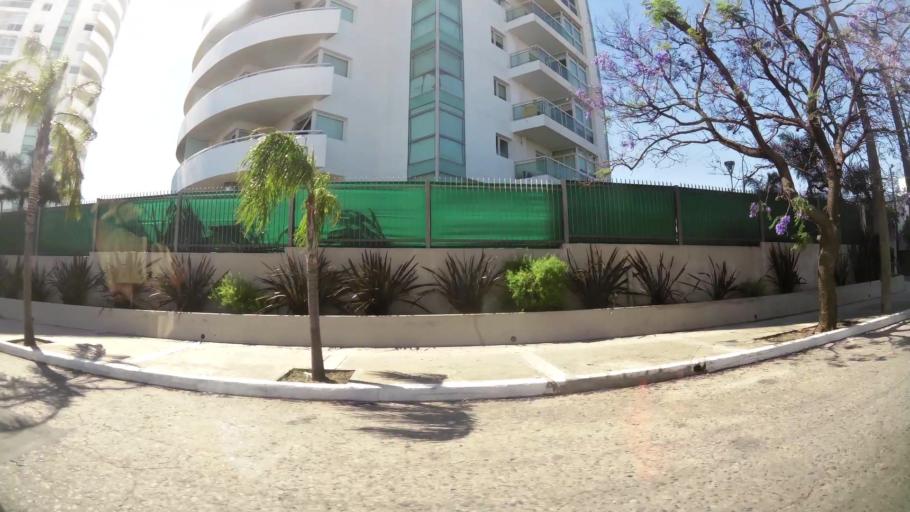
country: AR
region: Cordoba
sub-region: Departamento de Capital
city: Cordoba
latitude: -31.4062
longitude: -64.1678
